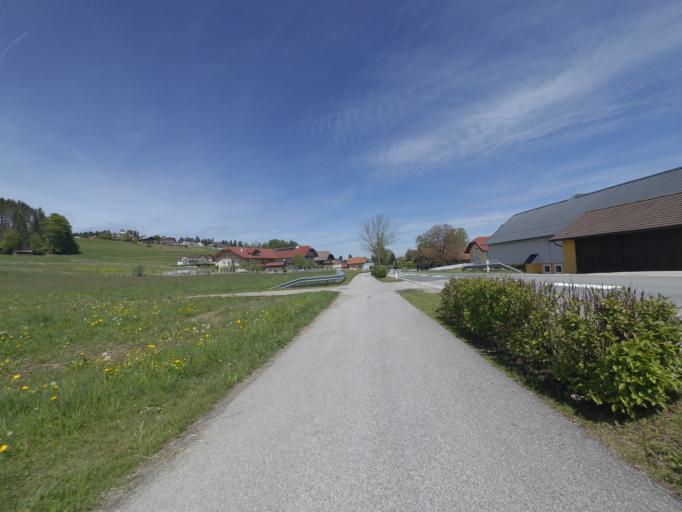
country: AT
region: Salzburg
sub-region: Politischer Bezirk Salzburg-Umgebung
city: Seeham
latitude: 47.9613
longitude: 13.0745
